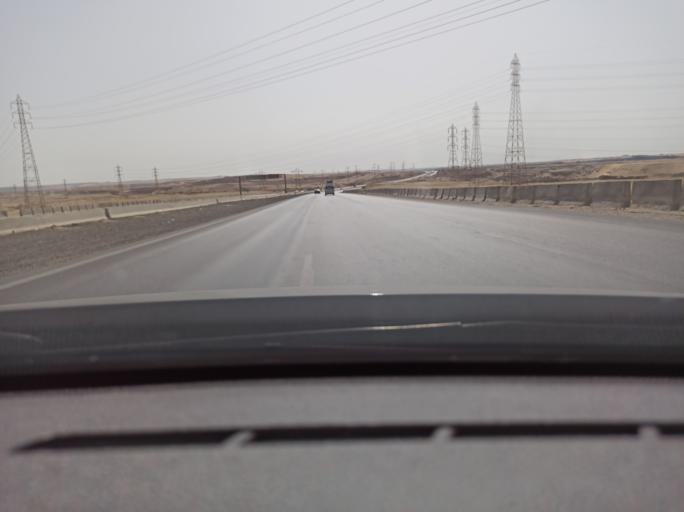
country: EG
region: Muhafazat al Qahirah
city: Halwan
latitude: 29.7841
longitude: 31.3576
